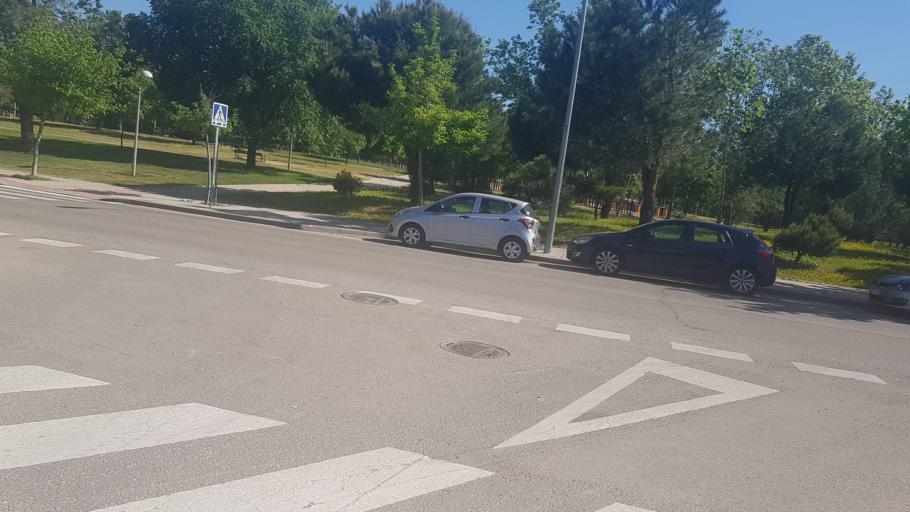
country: ES
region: Madrid
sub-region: Provincia de Madrid
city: Pozuelo de Alarcon
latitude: 40.4661
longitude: -3.7882
